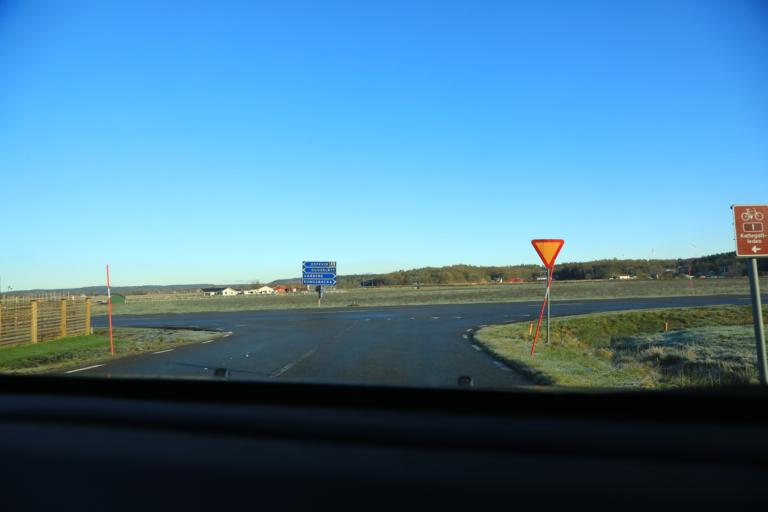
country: SE
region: Halland
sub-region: Varbergs Kommun
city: Varberg
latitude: 57.1955
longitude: 12.2174
